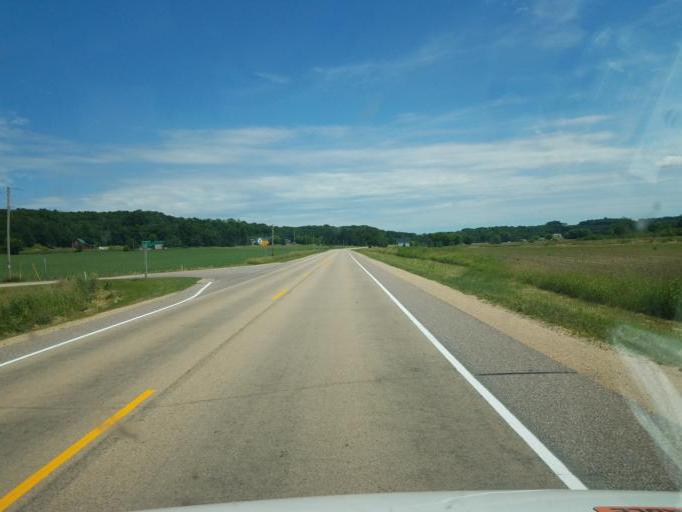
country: US
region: Wisconsin
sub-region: Sauk County
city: Reedsburg
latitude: 43.6180
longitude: -90.1483
